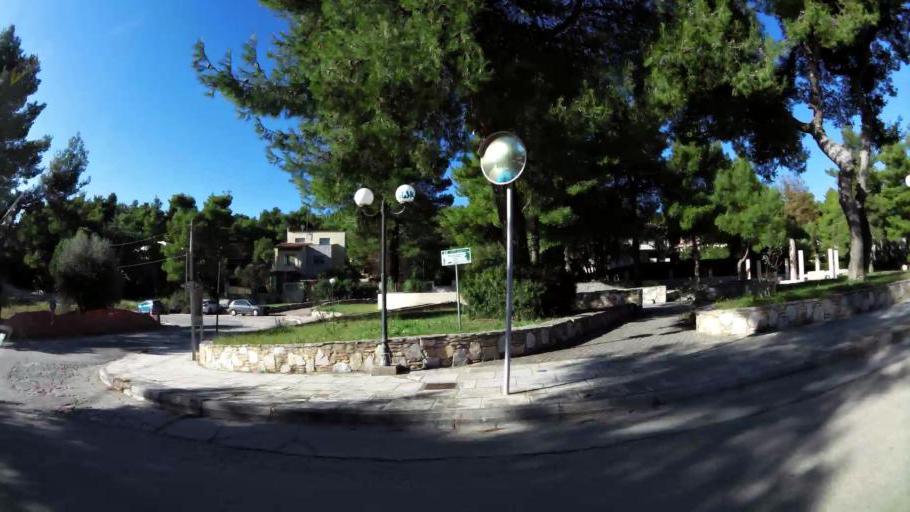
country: GR
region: Attica
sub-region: Nomarchia Anatolikis Attikis
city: Stamata
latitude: 38.1327
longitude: 23.8780
